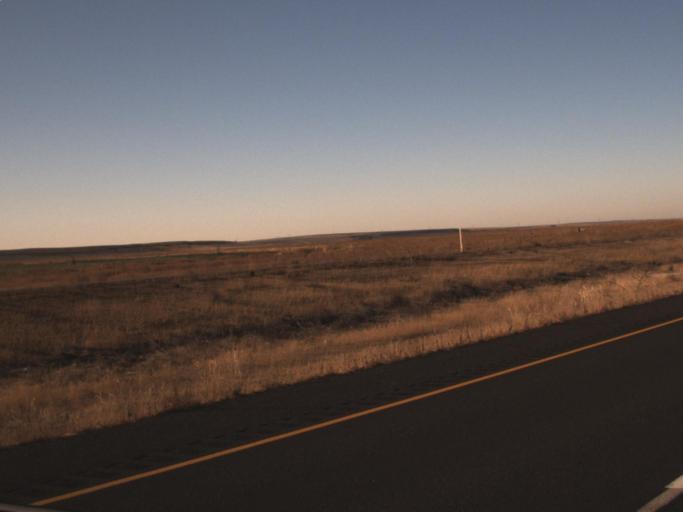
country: US
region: Washington
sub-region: Franklin County
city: Connell
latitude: 46.6190
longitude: -118.9000
